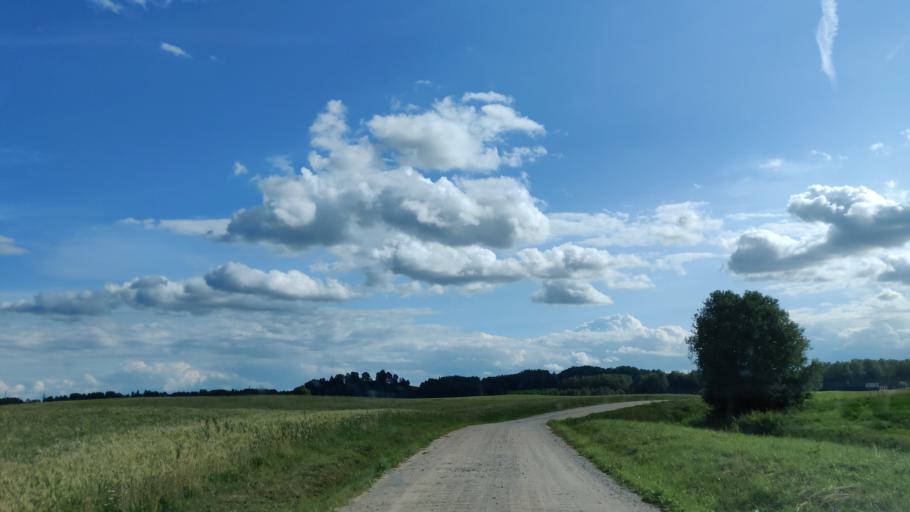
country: LT
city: Varniai
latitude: 55.6071
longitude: 22.3231
